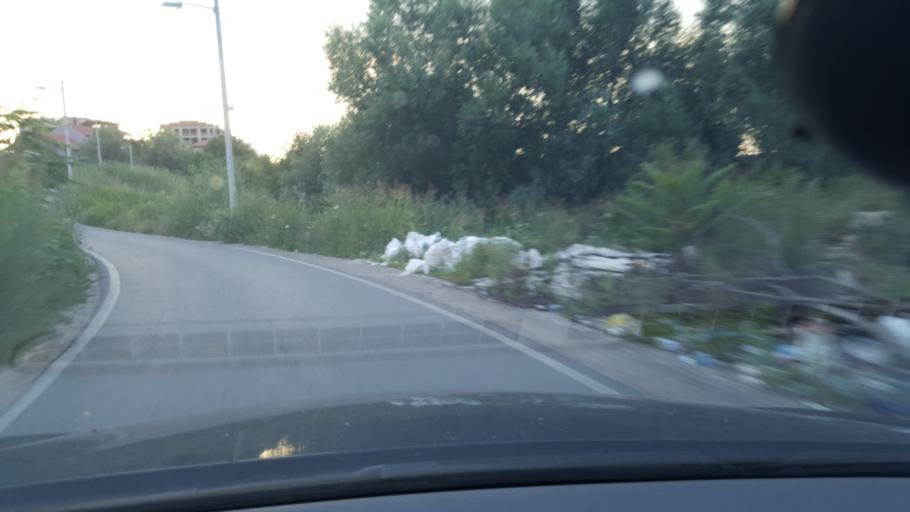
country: RS
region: Central Serbia
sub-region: Belgrade
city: Zvezdara
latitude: 44.7815
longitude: 20.5332
